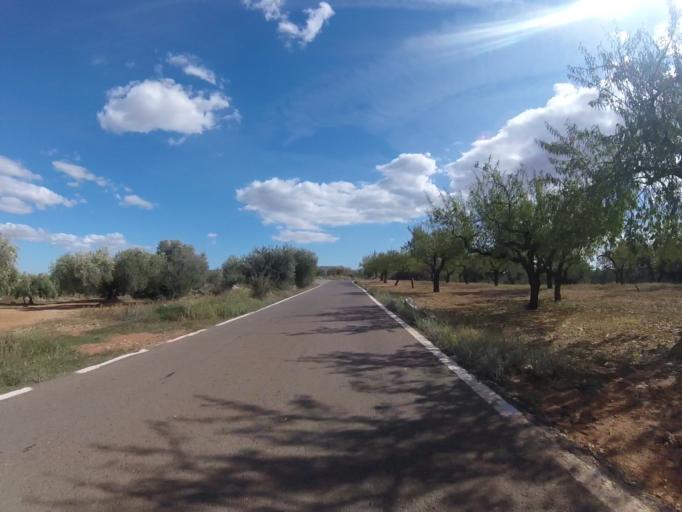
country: ES
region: Valencia
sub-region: Provincia de Castello
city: Cuevas de Vinroma
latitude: 40.3793
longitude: 0.1103
